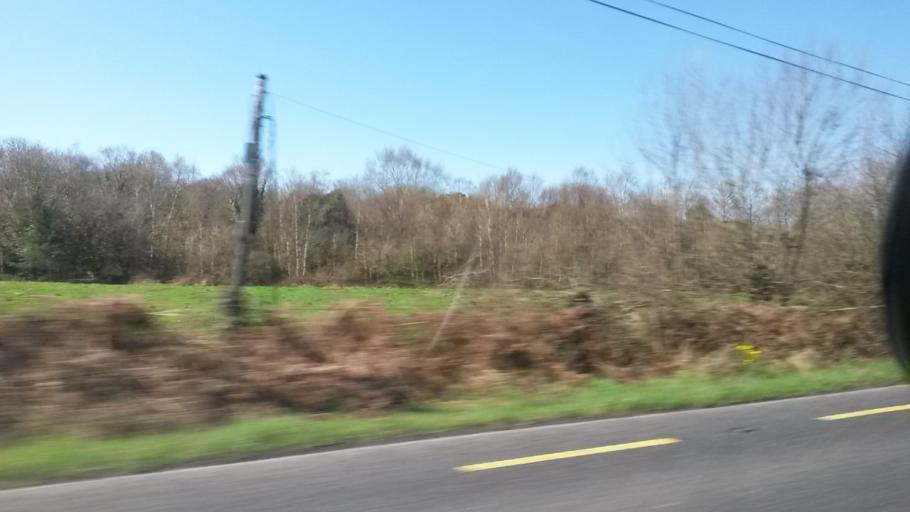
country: IE
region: Munster
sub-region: County Cork
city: Macroom
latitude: 51.9090
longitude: -9.0123
